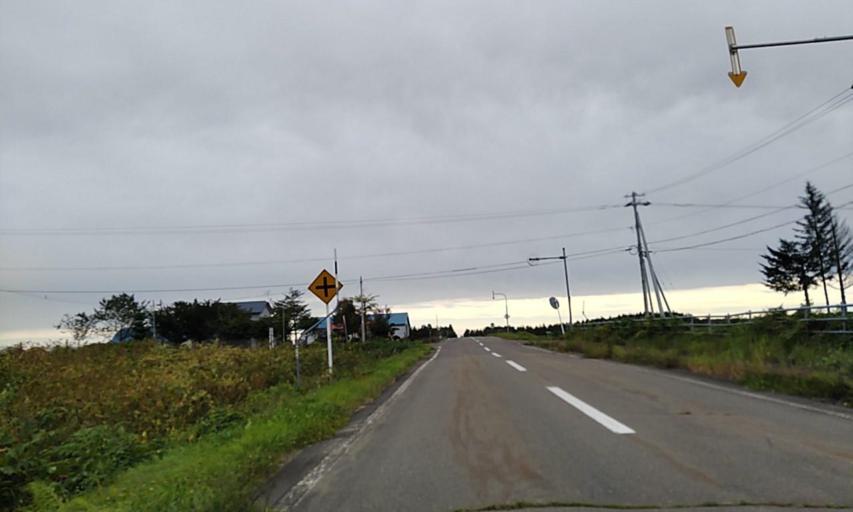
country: JP
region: Hokkaido
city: Obihiro
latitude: 42.6718
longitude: 143.0522
